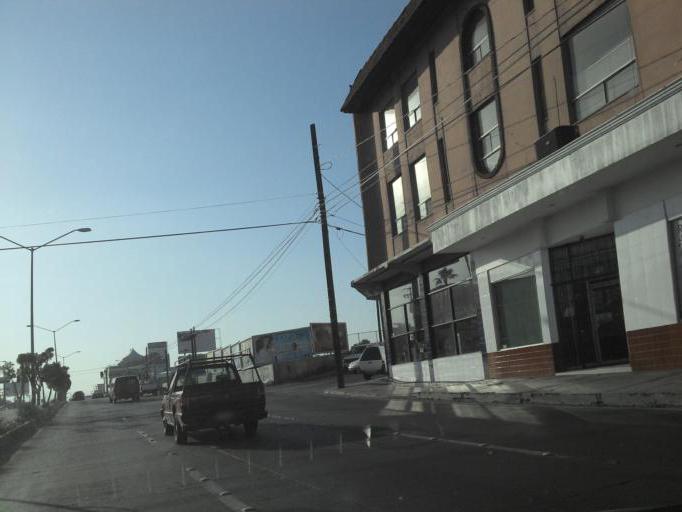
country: MX
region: Baja California
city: Tijuana
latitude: 32.5194
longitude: -117.0195
